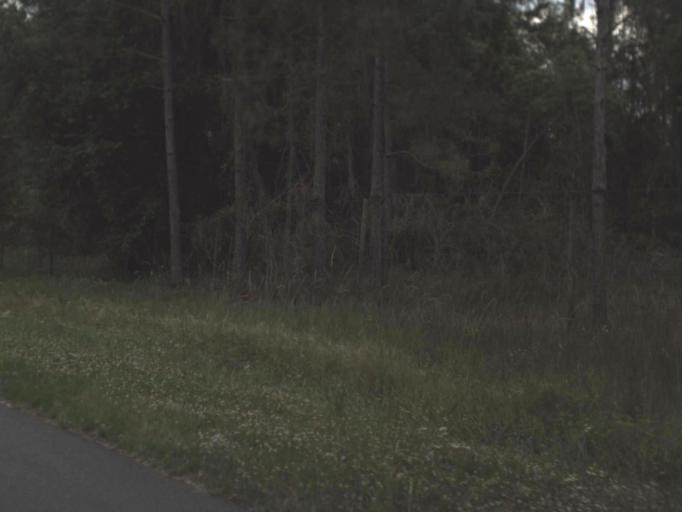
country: US
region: Florida
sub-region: Hamilton County
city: Jasper
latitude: 30.5253
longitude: -82.6739
